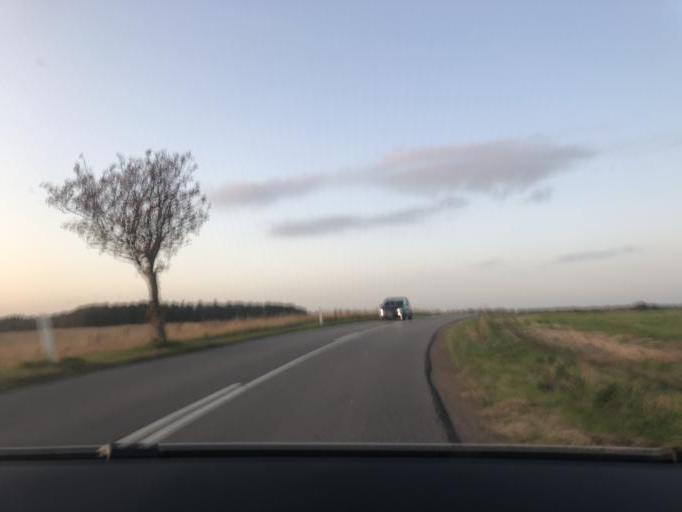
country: DK
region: Capital Region
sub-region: Egedal Kommune
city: Stenlose
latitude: 55.8035
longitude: 12.2117
